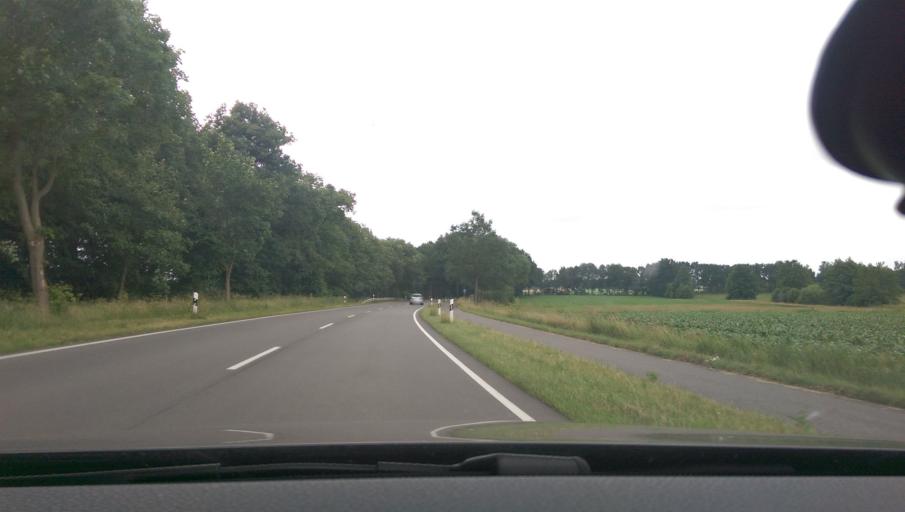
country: DE
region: Lower Saxony
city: Botersen
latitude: 53.1607
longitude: 9.3222
